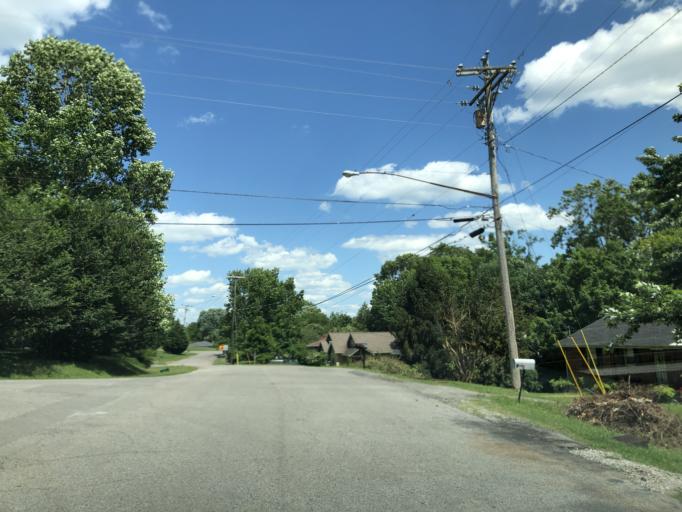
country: US
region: Tennessee
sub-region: Davidson County
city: Nashville
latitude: 36.1757
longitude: -86.7210
